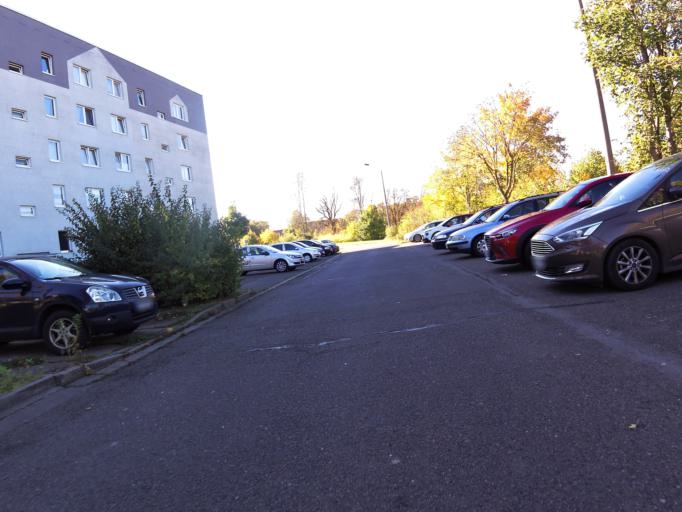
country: DE
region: Saxony
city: Leipzig
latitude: 51.3810
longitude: 12.3597
